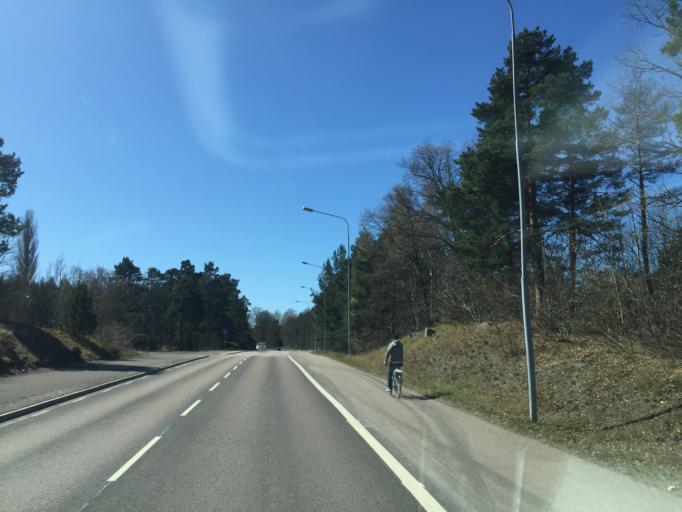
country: SE
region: Kalmar
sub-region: Oskarshamns Kommun
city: Oskarshamn
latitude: 57.2545
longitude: 16.4631
